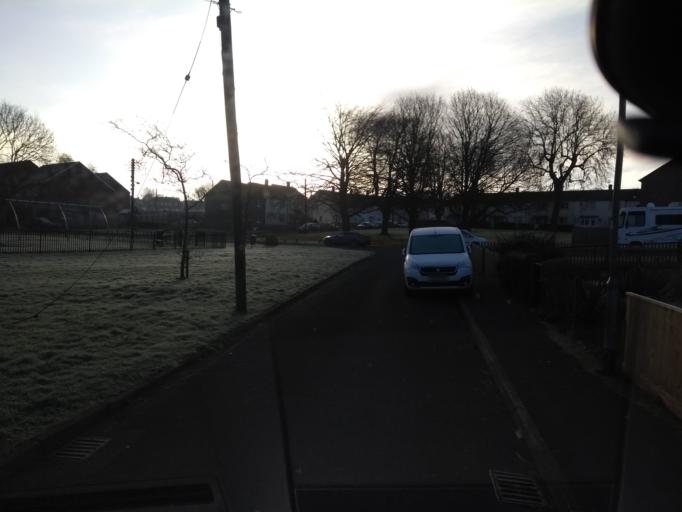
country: GB
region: England
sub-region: Somerset
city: Shepton Mallet
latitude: 51.1858
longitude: -2.5561
